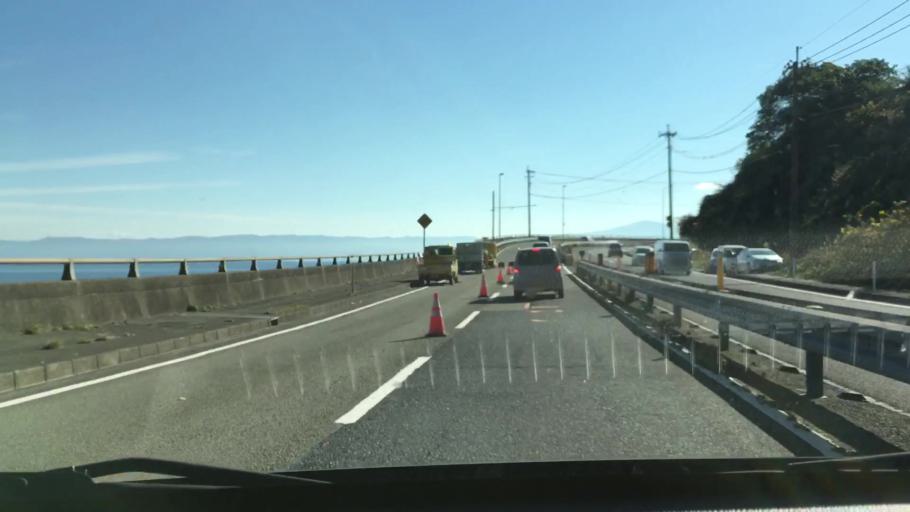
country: JP
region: Kagoshima
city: Kajiki
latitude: 31.6596
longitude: 130.6178
